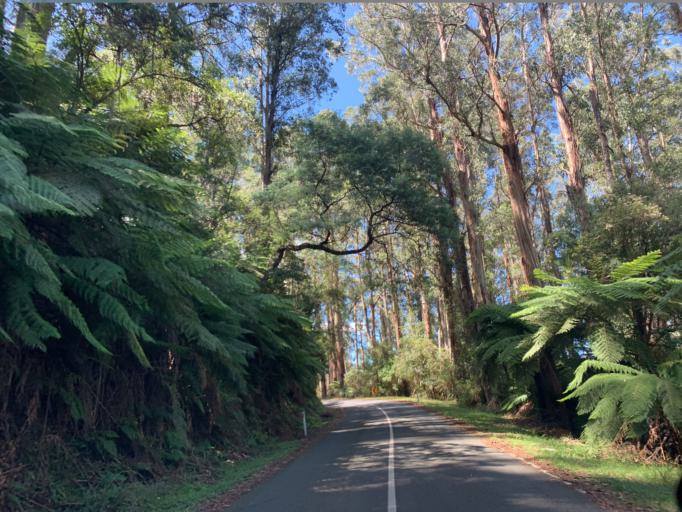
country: AU
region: Victoria
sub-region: Yarra Ranges
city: Millgrove
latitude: -37.7258
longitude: 145.7225
